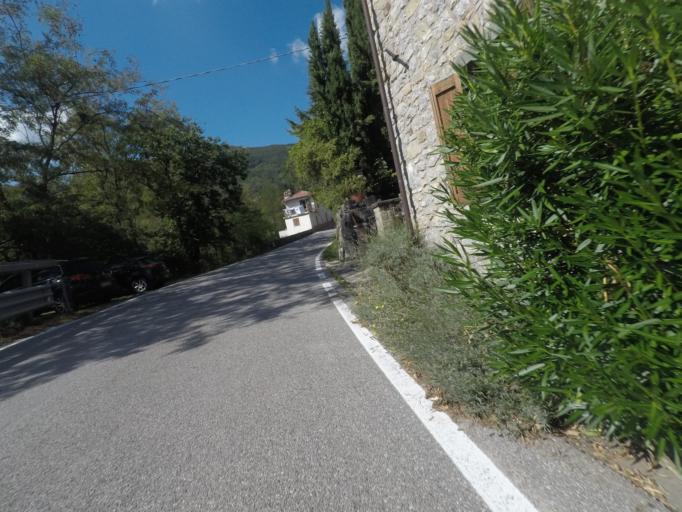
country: IT
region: Tuscany
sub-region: Provincia di Massa-Carrara
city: Fivizzano
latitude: 44.2528
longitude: 10.1738
